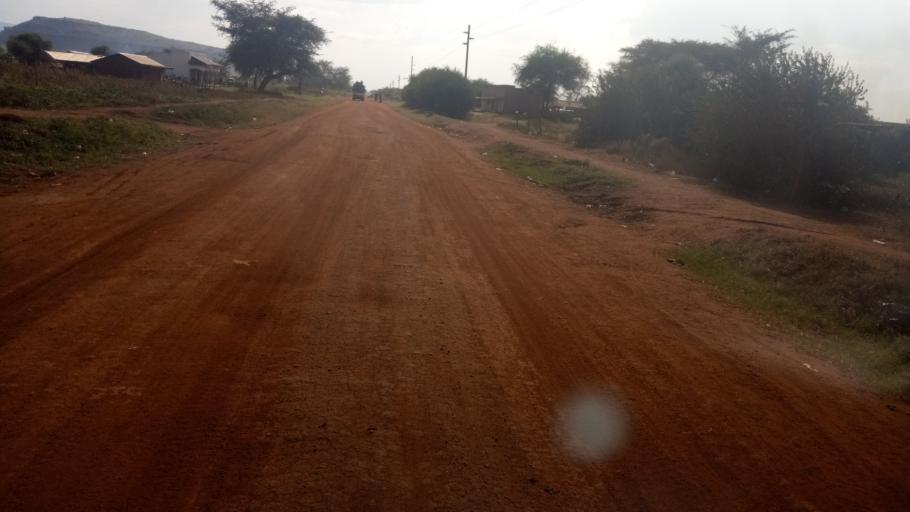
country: UG
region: Eastern Region
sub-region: Kween District
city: Binyin
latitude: 1.5248
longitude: 34.4878
